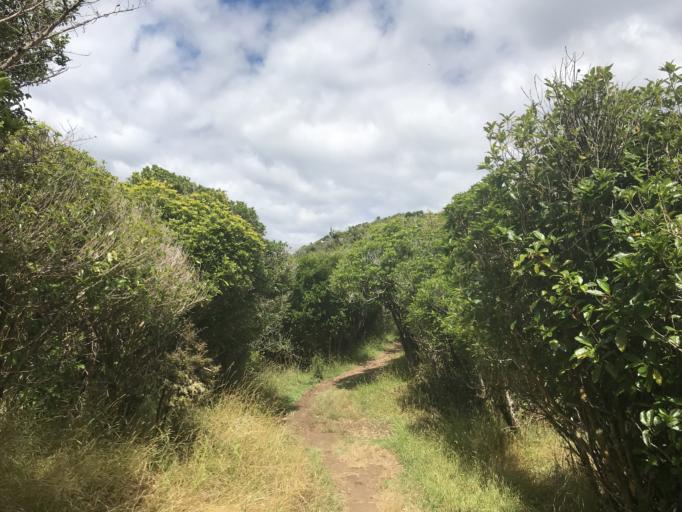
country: NZ
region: Marlborough
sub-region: Marlborough District
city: Picton
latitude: -41.2105
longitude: 174.0157
